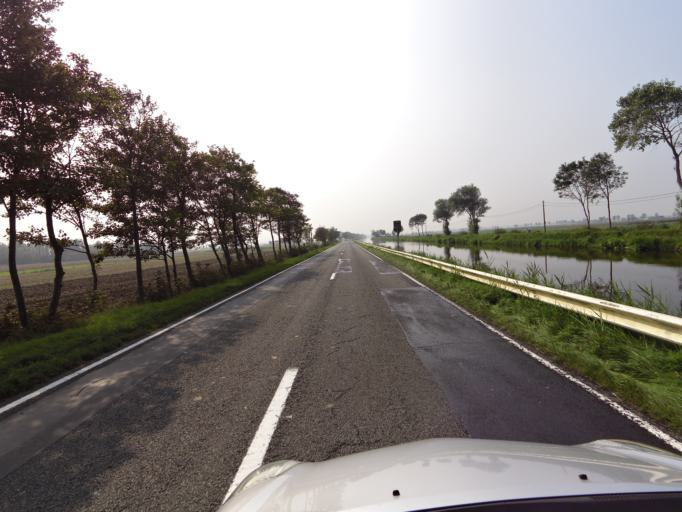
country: BE
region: Flanders
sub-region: Provincie West-Vlaanderen
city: Middelkerke
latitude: 51.1617
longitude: 2.8255
